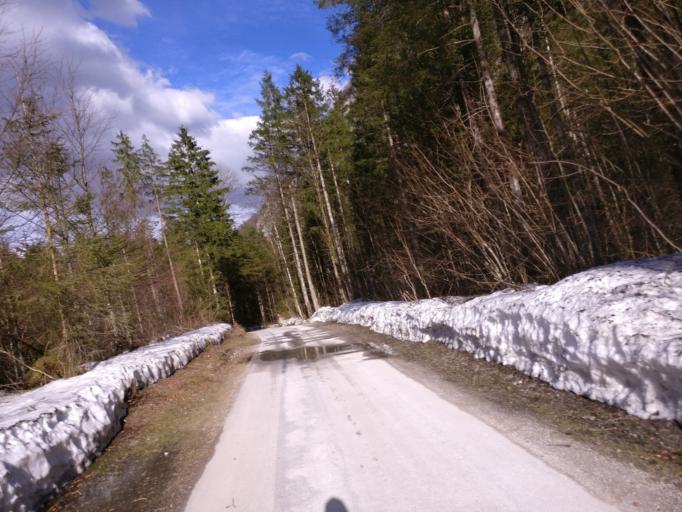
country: AT
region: Salzburg
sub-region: Politischer Bezirk Hallein
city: Golling an der Salzach
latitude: 47.5741
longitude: 13.1327
